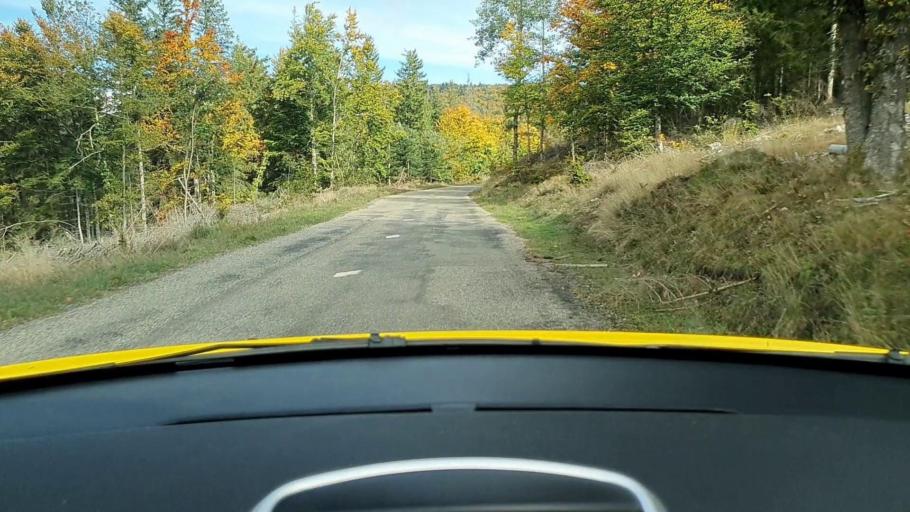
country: FR
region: Languedoc-Roussillon
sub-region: Departement du Gard
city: Valleraugue
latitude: 44.0575
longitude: 3.5713
